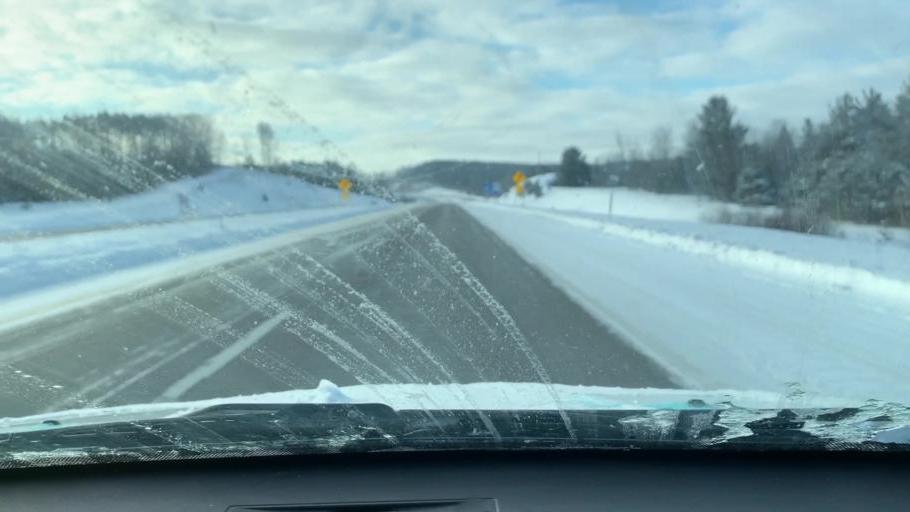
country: US
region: Michigan
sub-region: Wexford County
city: Cadillac
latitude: 44.3057
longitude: -85.3924
